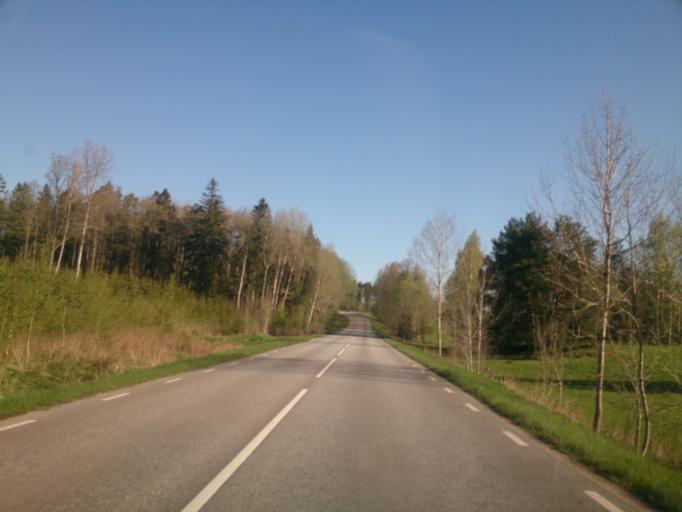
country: SE
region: OEstergoetland
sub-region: Linkopings Kommun
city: Berg
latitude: 58.5203
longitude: 15.5532
